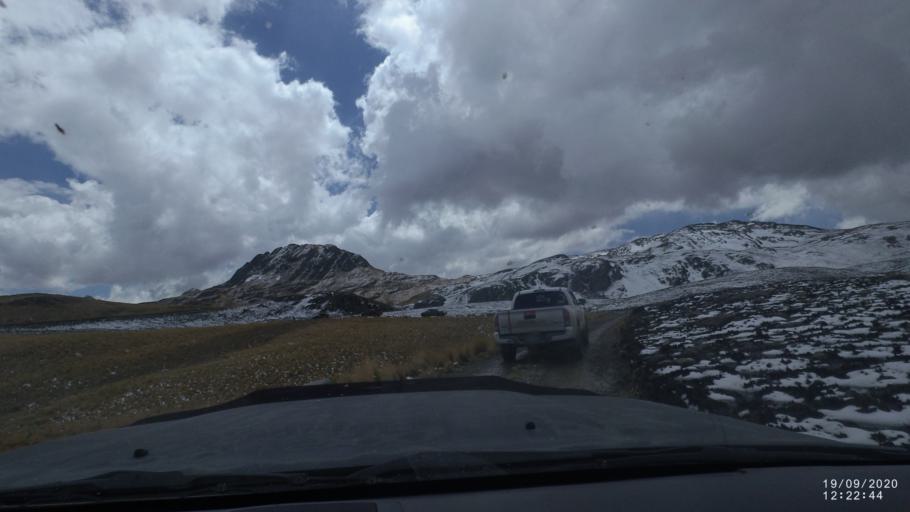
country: BO
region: Cochabamba
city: Cochabamba
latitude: -17.2963
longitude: -66.1086
